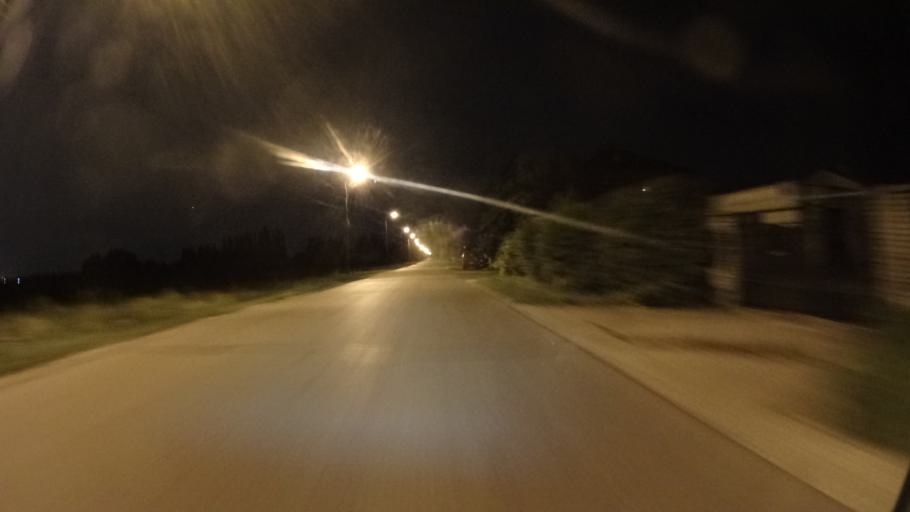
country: PL
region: Masovian Voivodeship
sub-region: Powiat warszawski zachodni
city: Hornowek
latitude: 52.2531
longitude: 20.7908
